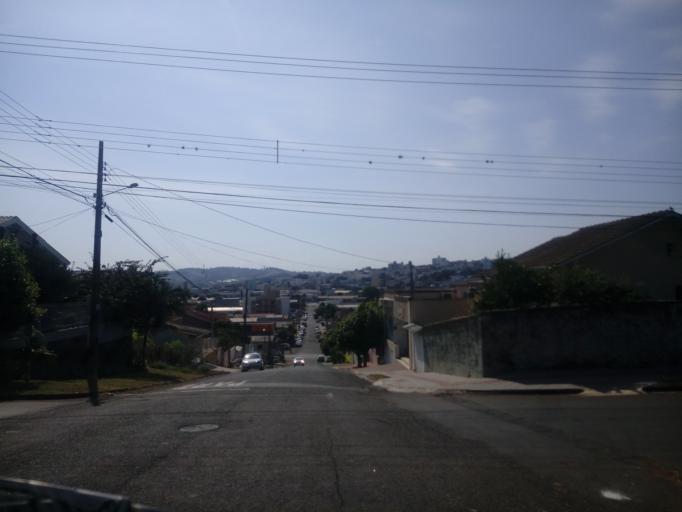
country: BR
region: Santa Catarina
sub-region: Chapeco
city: Chapeco
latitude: -27.0837
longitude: -52.6274
